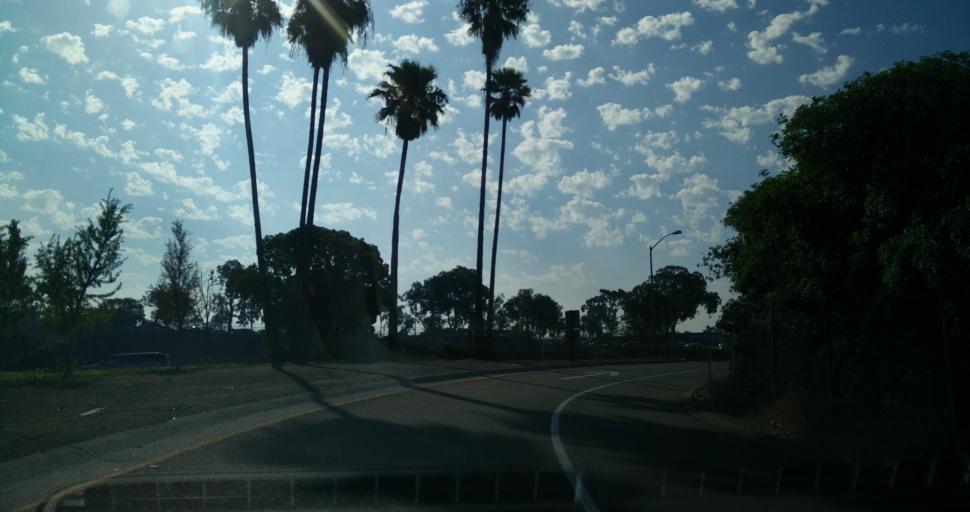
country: US
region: California
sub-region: San Diego County
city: San Diego
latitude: 32.7236
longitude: -117.1538
